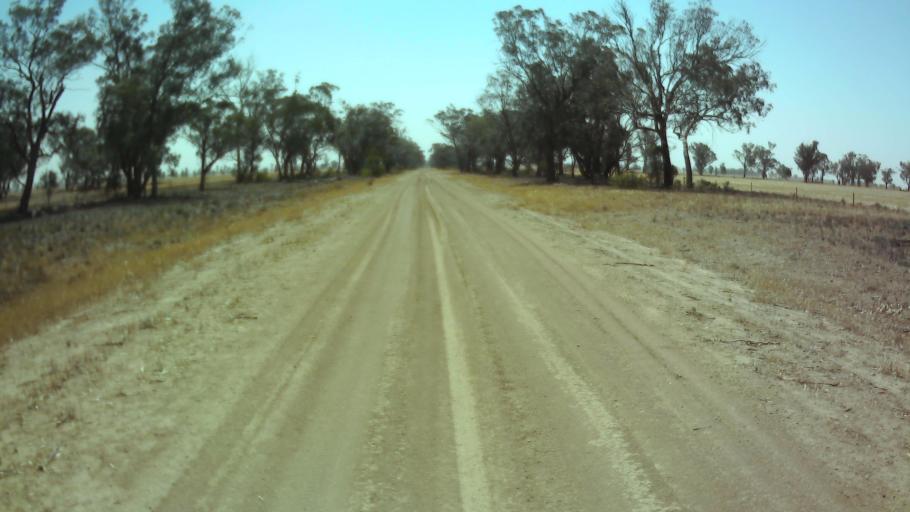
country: AU
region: New South Wales
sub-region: Weddin
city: Grenfell
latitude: -33.9351
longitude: 147.8053
